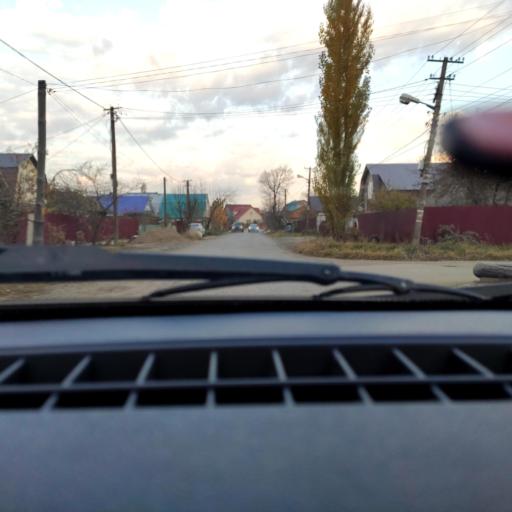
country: RU
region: Bashkortostan
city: Ufa
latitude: 54.8288
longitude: 56.1814
